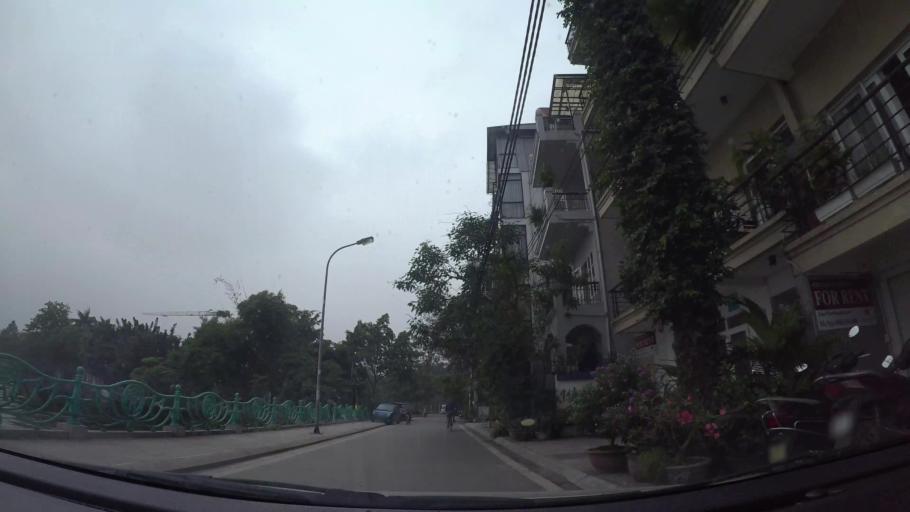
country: VN
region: Ha Noi
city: Tay Ho
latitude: 21.0616
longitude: 105.8201
